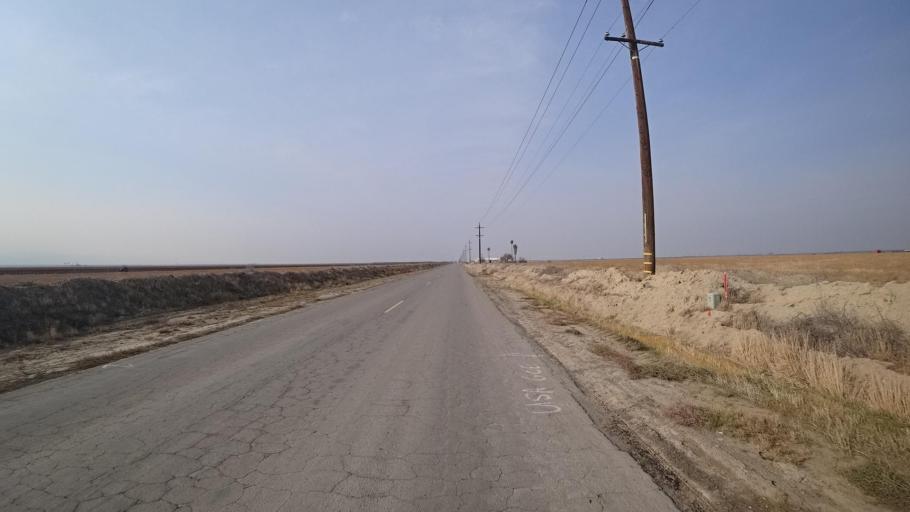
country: US
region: California
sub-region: Kern County
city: Greenfield
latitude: 35.0948
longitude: -119.0657
